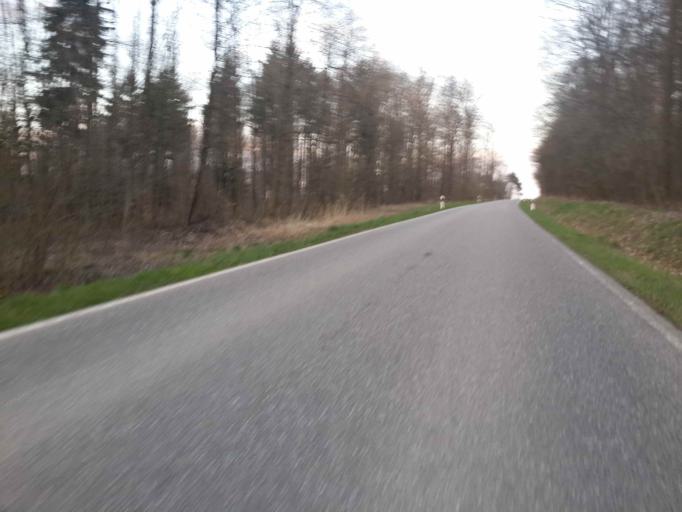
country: DE
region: Baden-Wuerttemberg
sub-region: Regierungsbezirk Stuttgart
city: Kirchardt
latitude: 49.2433
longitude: 9.0300
